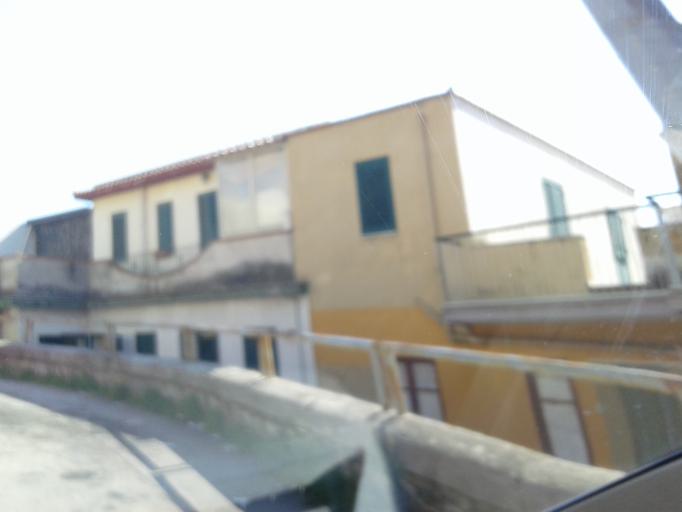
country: IT
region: Sicily
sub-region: Palermo
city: Piano dei Geli
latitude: 38.1091
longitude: 13.3069
